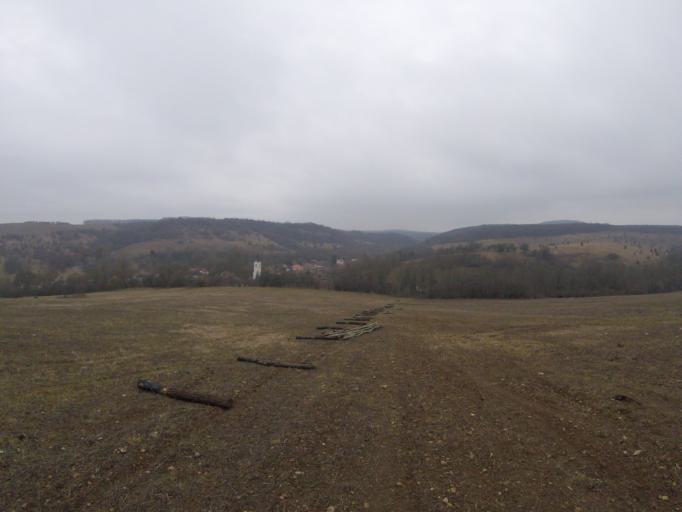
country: HU
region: Borsod-Abauj-Zemplen
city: Rudabanya
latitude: 48.4448
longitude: 20.5907
